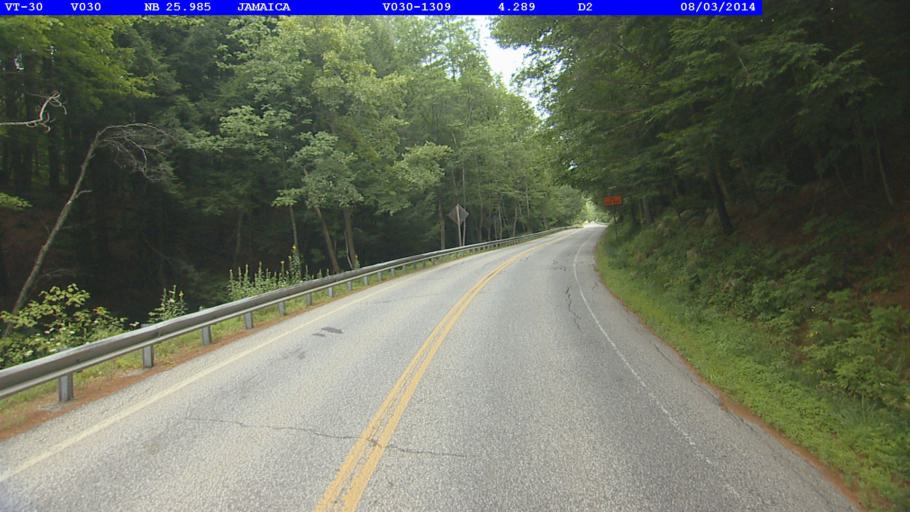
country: US
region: Vermont
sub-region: Windham County
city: Dover
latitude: 43.0982
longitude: -72.7876
